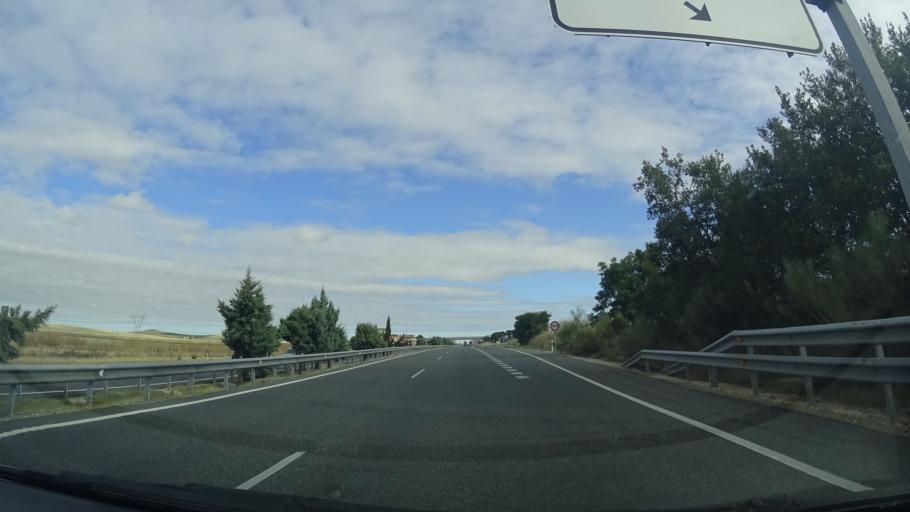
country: ES
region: Castille and Leon
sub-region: Provincia de Valladolid
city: Ataquines
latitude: 41.1736
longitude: -4.8035
